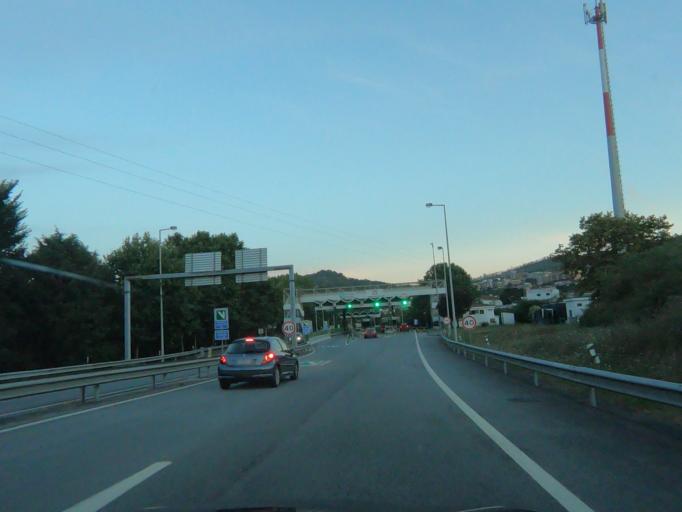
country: PT
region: Porto
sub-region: Valongo
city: Valongo
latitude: 41.1958
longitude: -8.5049
